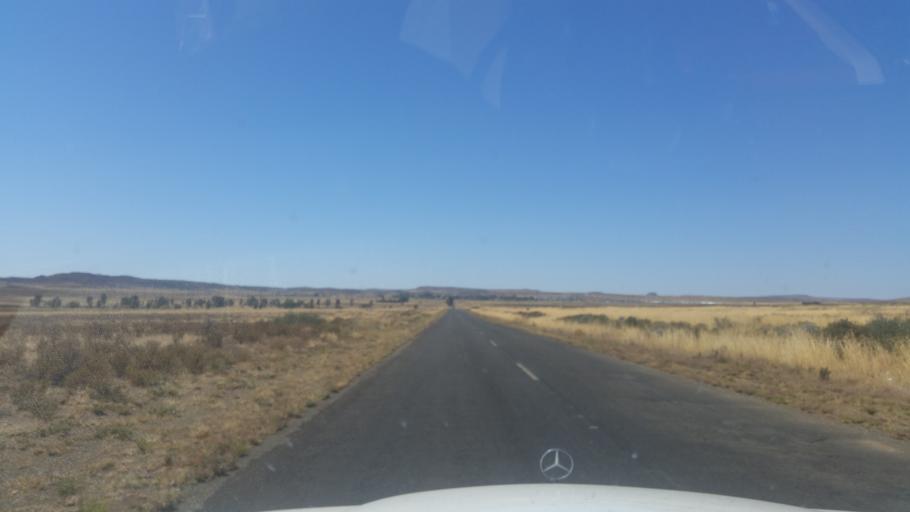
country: ZA
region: Eastern Cape
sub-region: Joe Gqabi District Municipality
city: Burgersdorp
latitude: -30.7499
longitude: 25.7662
